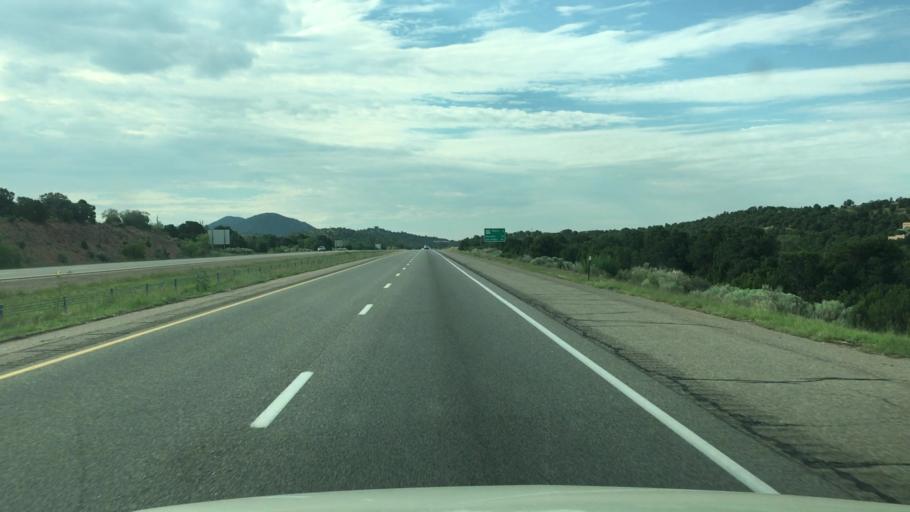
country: US
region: New Mexico
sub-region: Santa Fe County
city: Santa Fe
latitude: 35.6301
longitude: -105.9242
